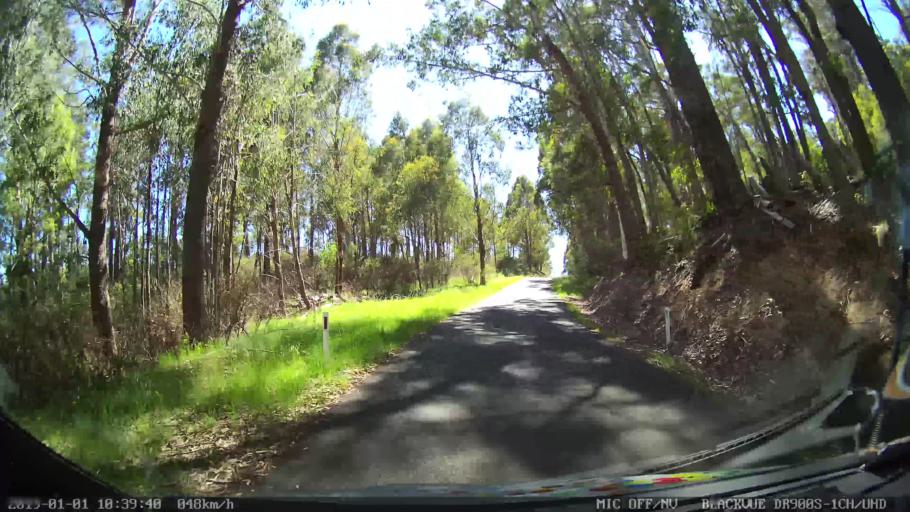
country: AU
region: New South Wales
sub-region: Snowy River
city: Jindabyne
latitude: -36.0396
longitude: 148.3066
